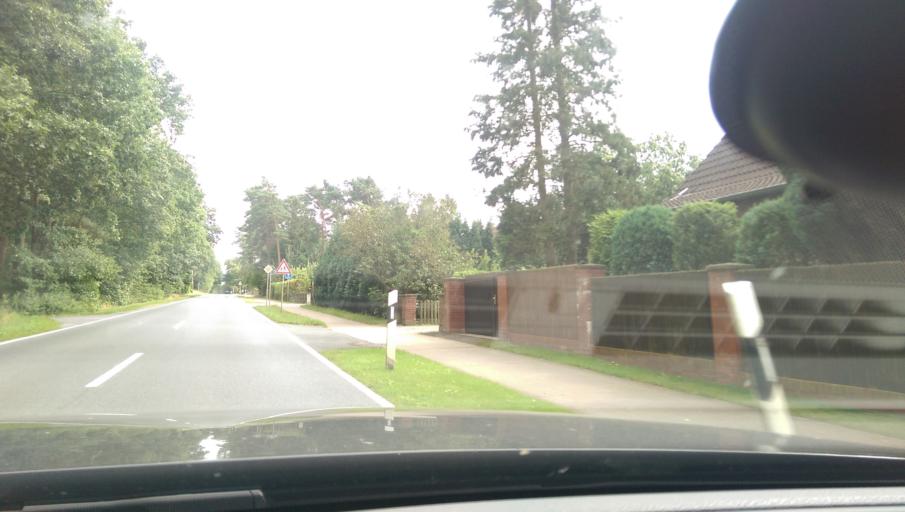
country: DE
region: Lower Saxony
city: Lindwedel
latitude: 52.5788
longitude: 9.5940
